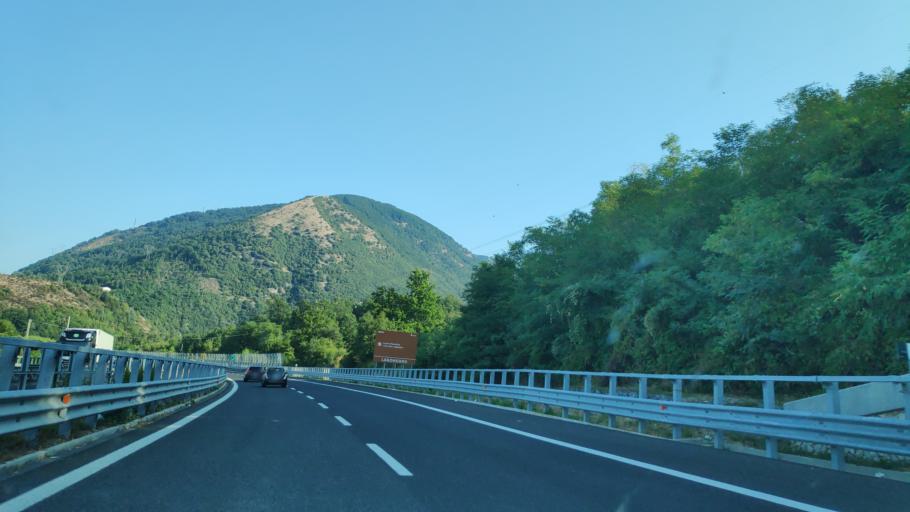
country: IT
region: Basilicate
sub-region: Provincia di Potenza
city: Lagonegro
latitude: 40.1206
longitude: 15.7841
